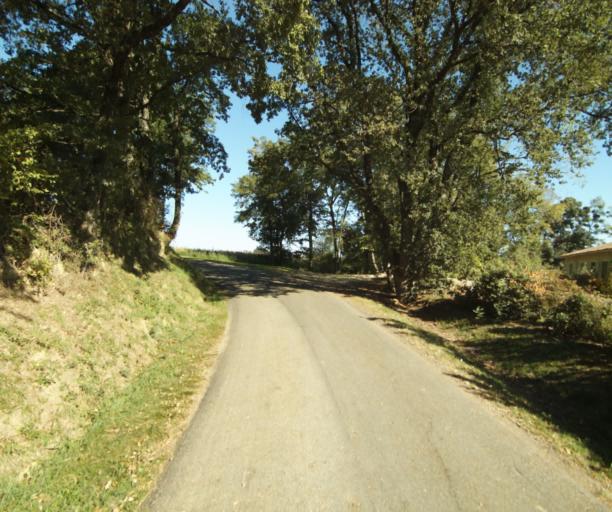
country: FR
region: Midi-Pyrenees
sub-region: Departement du Gers
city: Eauze
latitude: 43.8130
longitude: 0.1652
